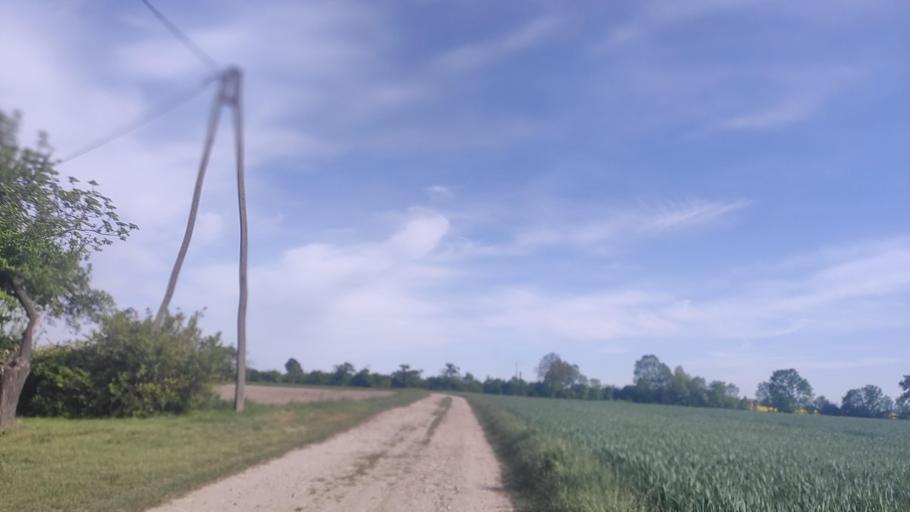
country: PL
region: Greater Poland Voivodeship
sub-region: Powiat poznanski
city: Swarzedz
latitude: 52.4140
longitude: 17.1523
